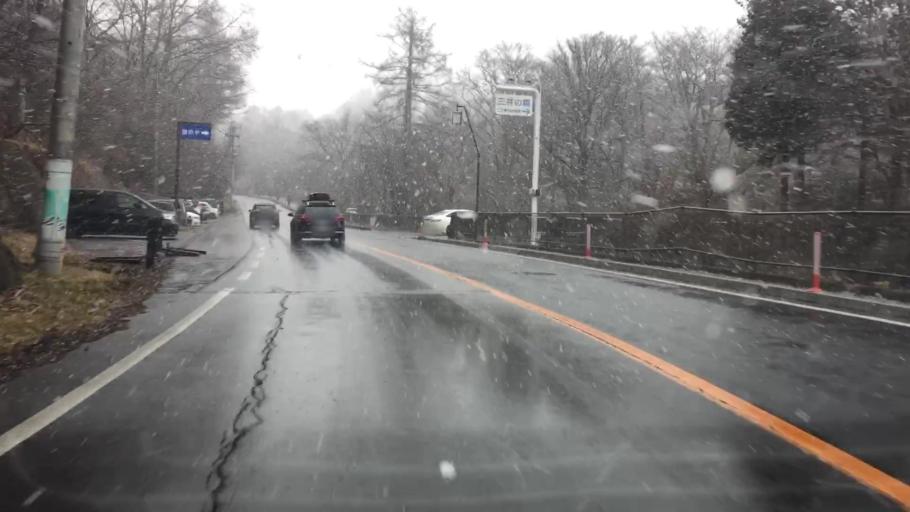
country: JP
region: Nagano
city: Komoro
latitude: 36.3572
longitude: 138.5902
